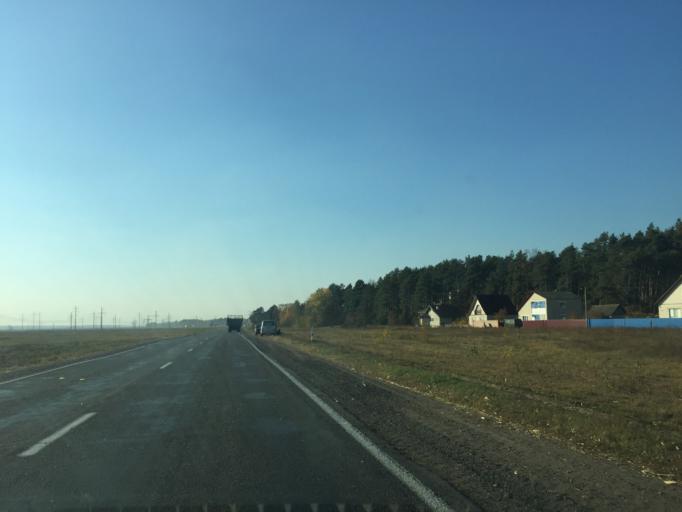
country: BY
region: Gomel
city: Dobrush
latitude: 52.3839
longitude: 31.3052
